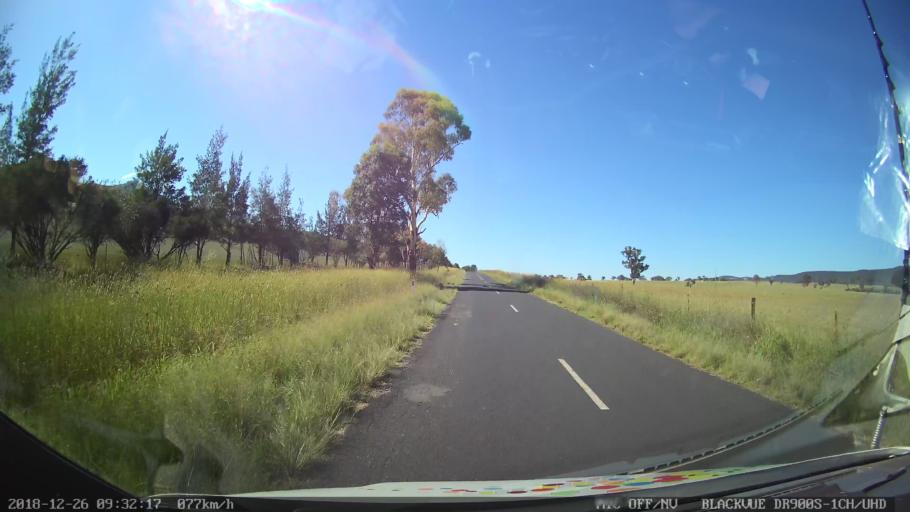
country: AU
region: New South Wales
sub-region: Mid-Western Regional
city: Kandos
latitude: -32.8825
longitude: 150.0322
